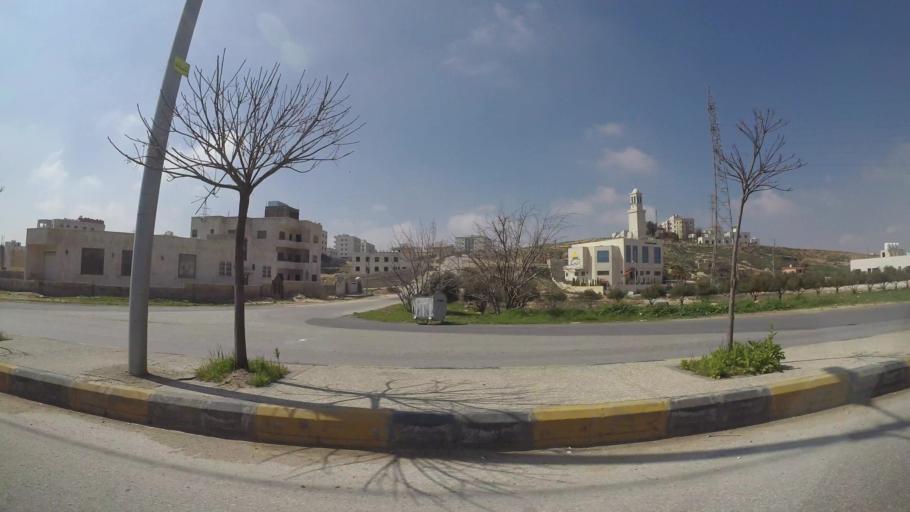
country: JO
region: Amman
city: Al Bunayyat ash Shamaliyah
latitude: 31.8917
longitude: 35.9030
